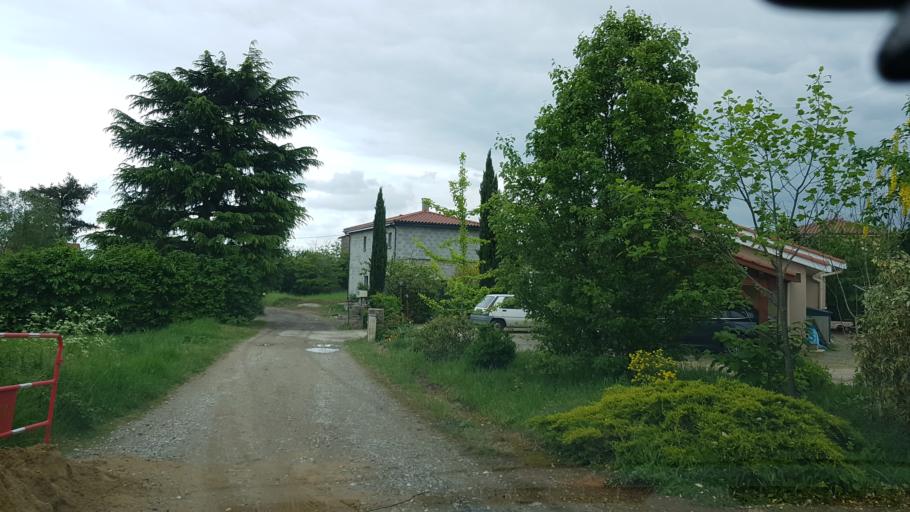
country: FR
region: Rhone-Alpes
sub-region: Departement du Rhone
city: Mornant
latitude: 45.6266
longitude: 4.6639
